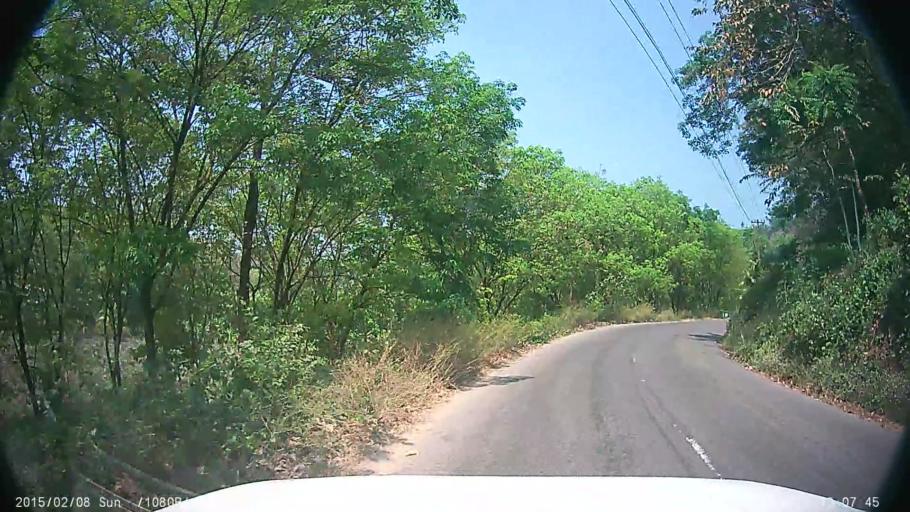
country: IN
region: Kerala
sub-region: Ernakulam
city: Muvattupuzha
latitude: 9.9189
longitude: 76.5822
